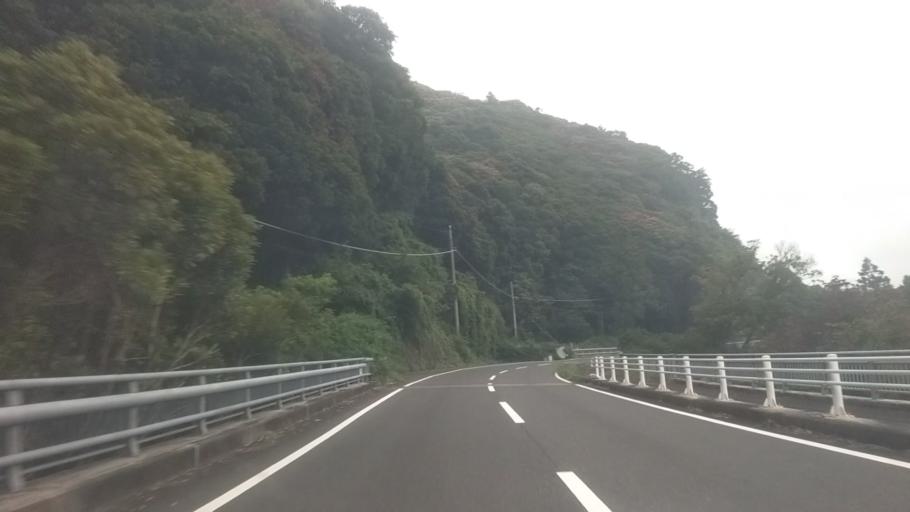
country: JP
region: Chiba
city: Kawaguchi
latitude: 35.1416
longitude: 140.1497
